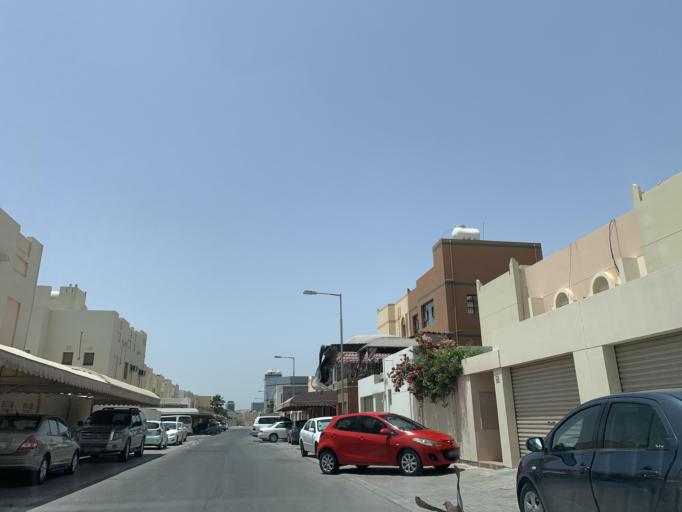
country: BH
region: Northern
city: Sitrah
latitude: 26.1416
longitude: 50.5922
